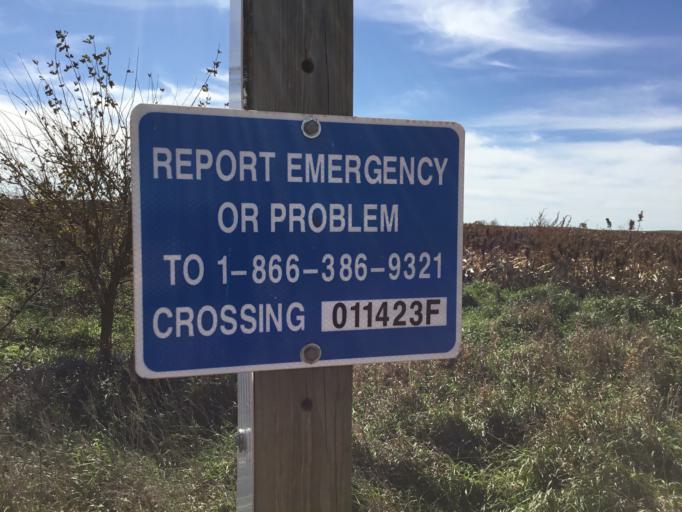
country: US
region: Kansas
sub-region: Lincoln County
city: Lincoln
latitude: 38.9582
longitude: -98.0310
